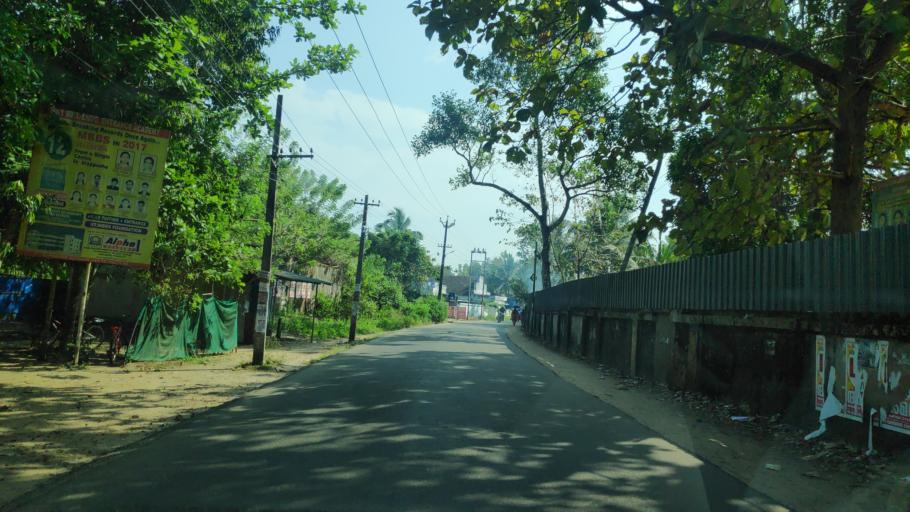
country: IN
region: Kerala
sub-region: Alappuzha
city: Alleppey
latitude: 9.5659
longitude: 76.3089
